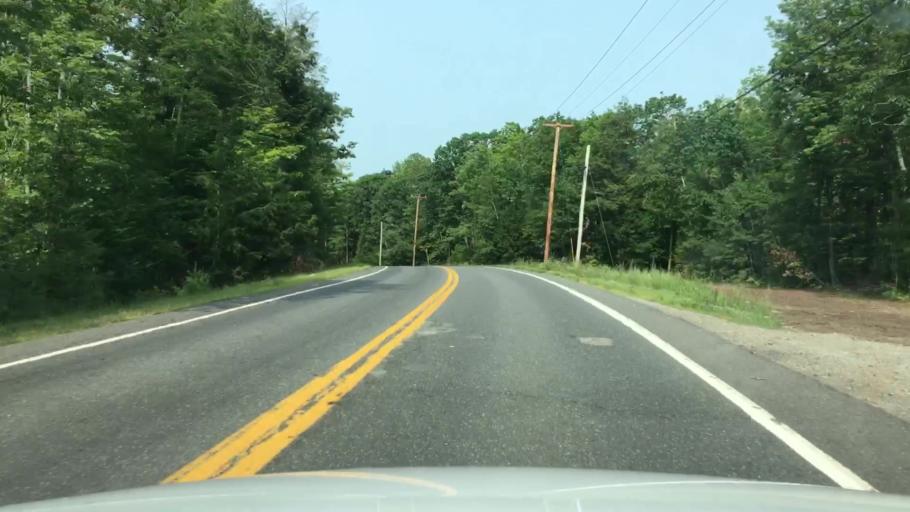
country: US
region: Maine
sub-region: Kennebec County
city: Augusta
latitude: 44.3169
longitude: -69.7229
